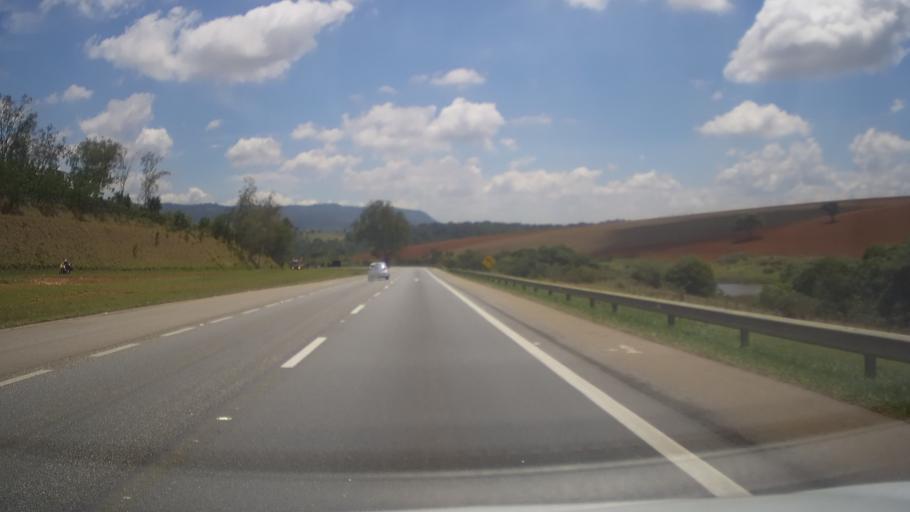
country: BR
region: Minas Gerais
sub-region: Sao Goncalo Do Sapucai
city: Sao Goncalo do Sapucai
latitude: -21.9307
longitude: -45.6118
